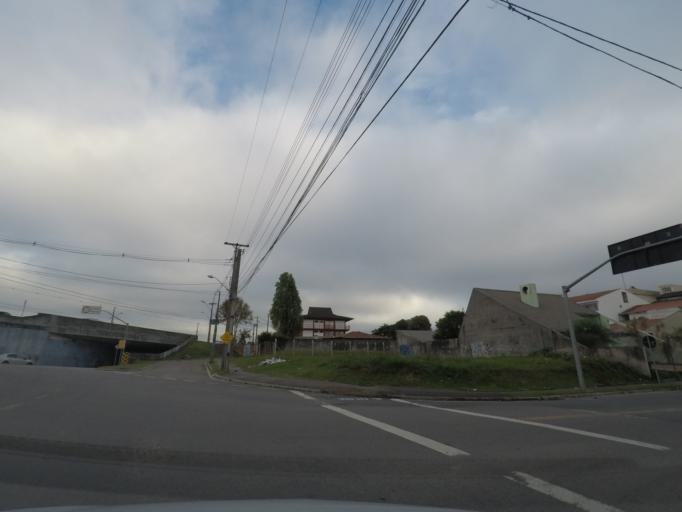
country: BR
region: Parana
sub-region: Curitiba
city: Curitiba
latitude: -25.4447
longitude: -49.2485
